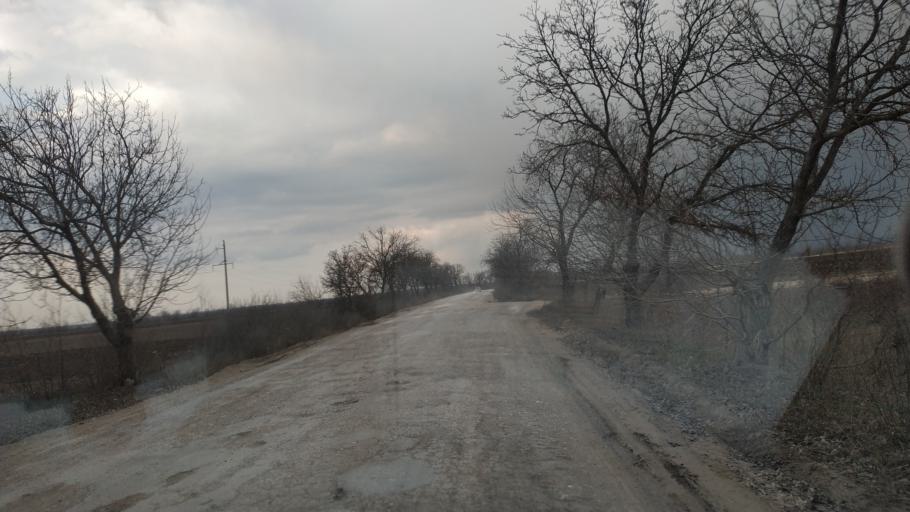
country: MD
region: Telenesti
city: Grigoriopol
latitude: 47.0523
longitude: 29.2938
